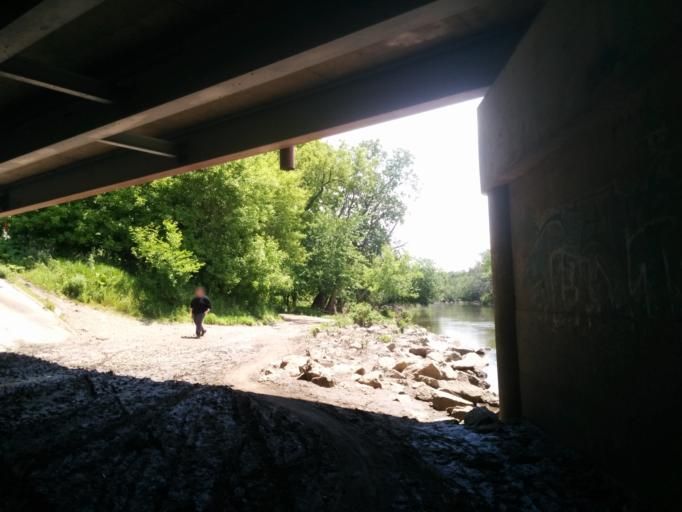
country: US
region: Illinois
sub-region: Cook County
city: Franklin Park
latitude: 41.9374
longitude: -87.8494
